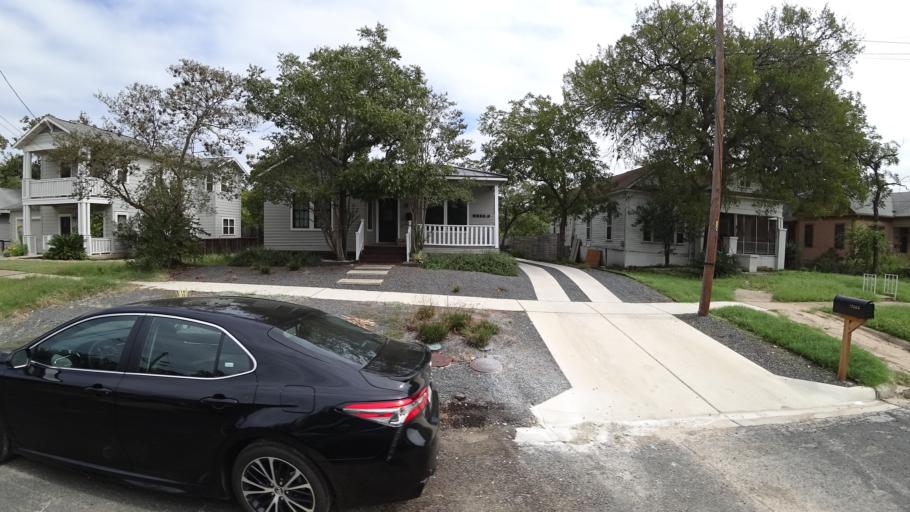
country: US
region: Texas
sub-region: Travis County
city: Austin
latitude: 30.2719
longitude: -97.7263
